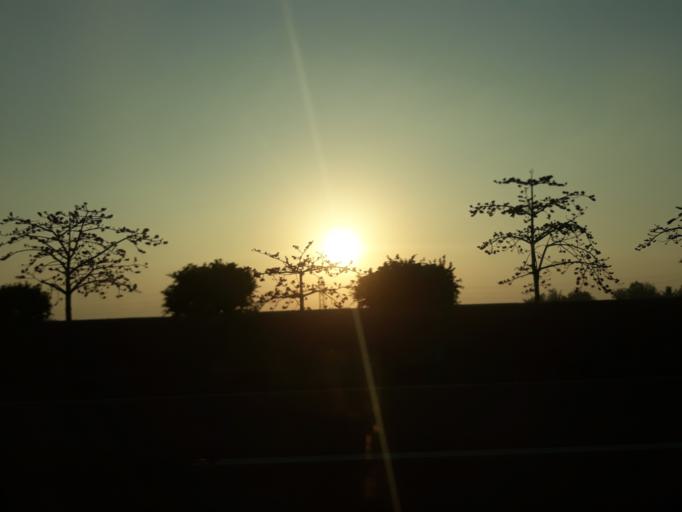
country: TW
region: Taiwan
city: Fengshan
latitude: 22.7696
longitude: 120.3275
